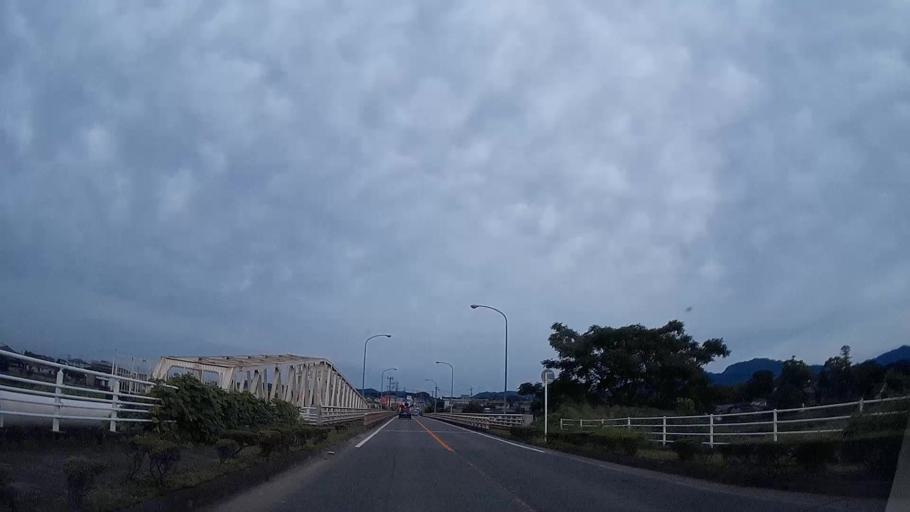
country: JP
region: Kumamoto
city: Kikuchi
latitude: 32.9700
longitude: 130.8110
